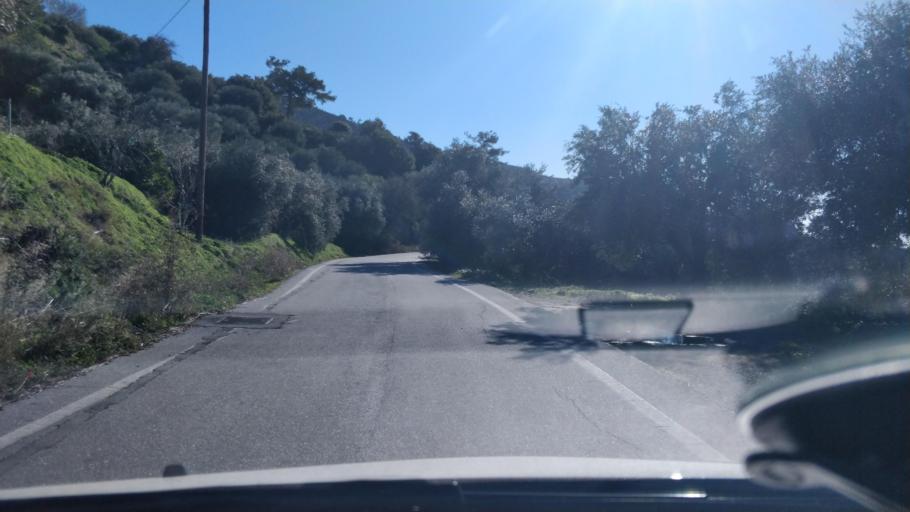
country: GR
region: Crete
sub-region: Nomos Lasithiou
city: Kritsa
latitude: 35.0789
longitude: 25.5970
